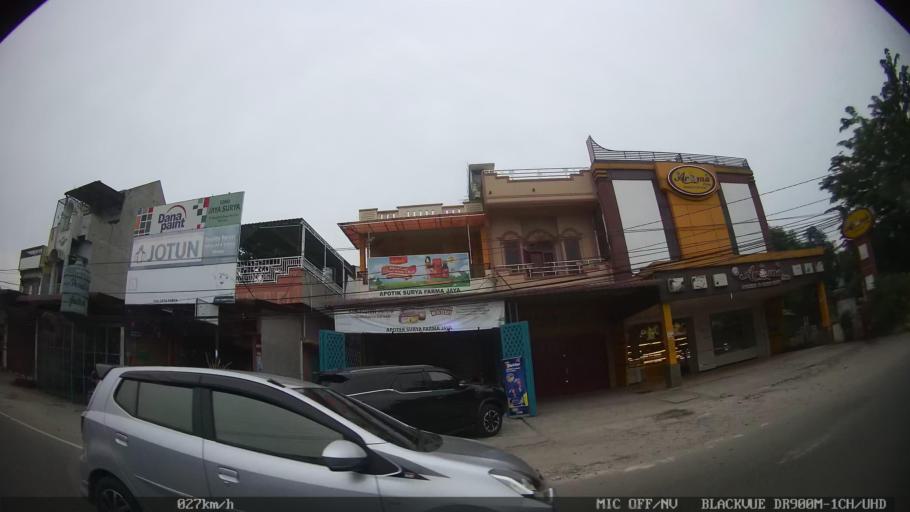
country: ID
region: North Sumatra
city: Deli Tua
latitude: 3.5507
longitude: 98.7171
